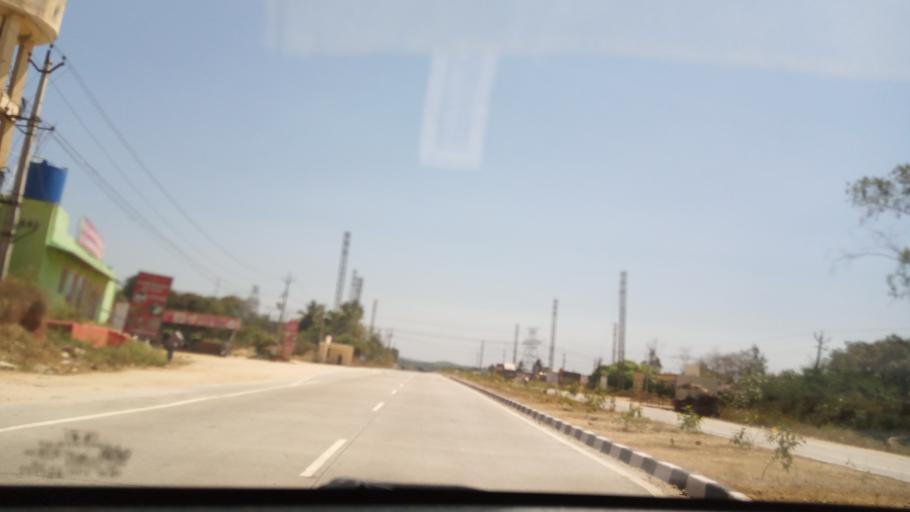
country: IN
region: Andhra Pradesh
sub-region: Chittoor
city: Chittoor
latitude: 13.1977
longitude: 78.9788
